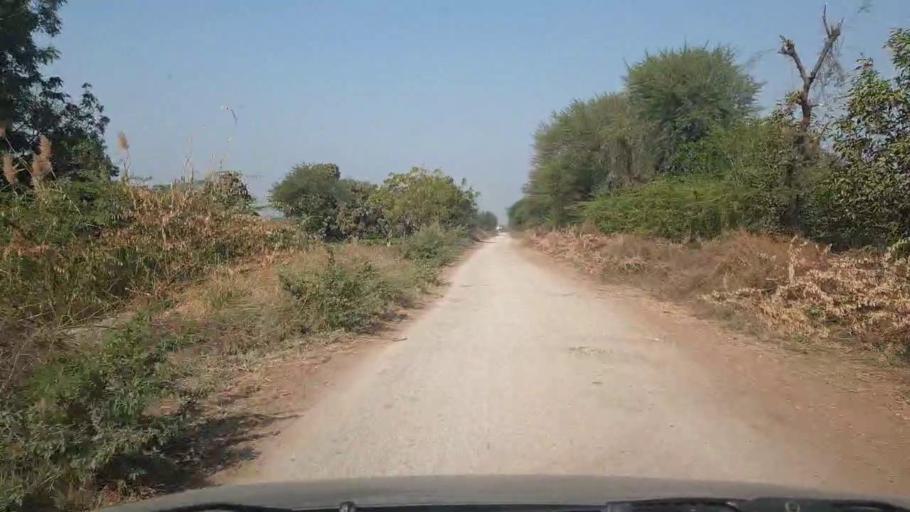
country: PK
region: Sindh
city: Mirwah Gorchani
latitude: 25.2782
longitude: 69.1313
